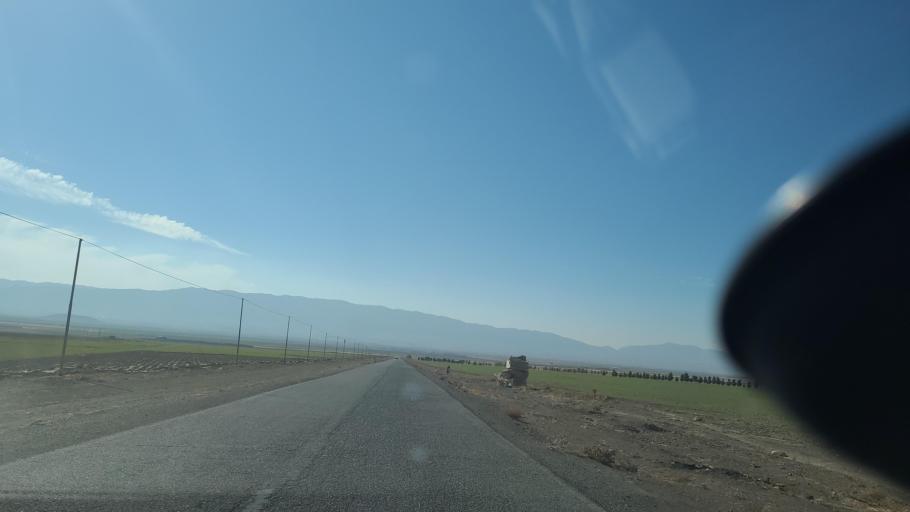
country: IR
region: Razavi Khorasan
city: Dowlatabad
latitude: 35.6091
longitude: 59.4673
